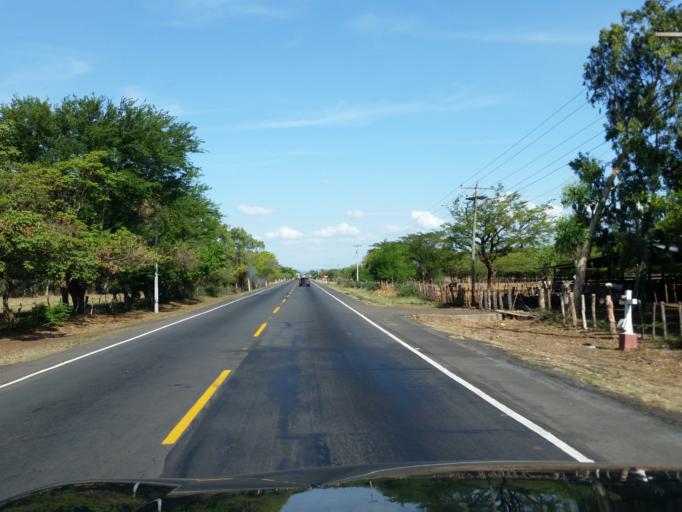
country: NI
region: Leon
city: La Paz Centro
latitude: 12.3215
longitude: -86.7956
